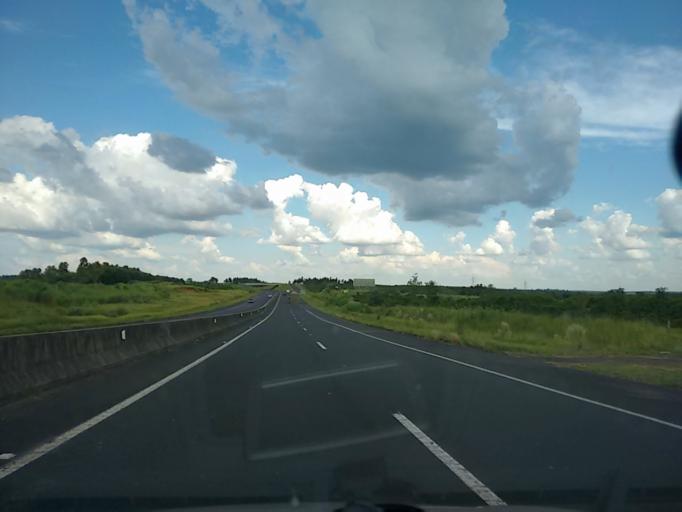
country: BR
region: Sao Paulo
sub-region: Garca
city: Garca
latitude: -22.2265
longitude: -49.7792
